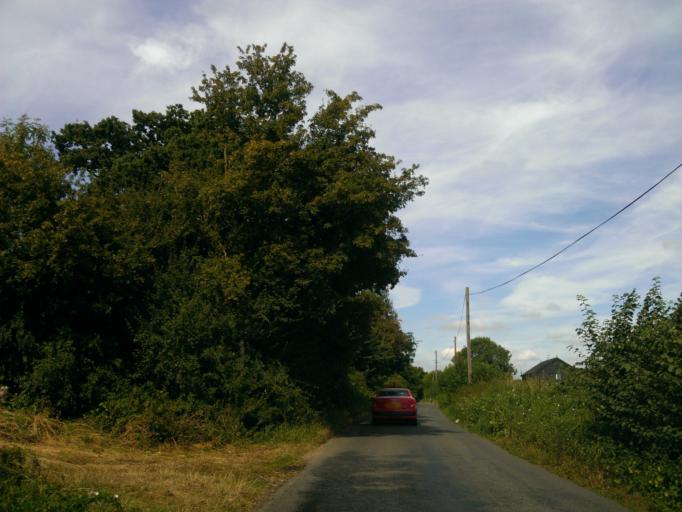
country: GB
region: England
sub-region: Essex
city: Sible Hedingham
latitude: 51.9753
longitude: 0.6176
